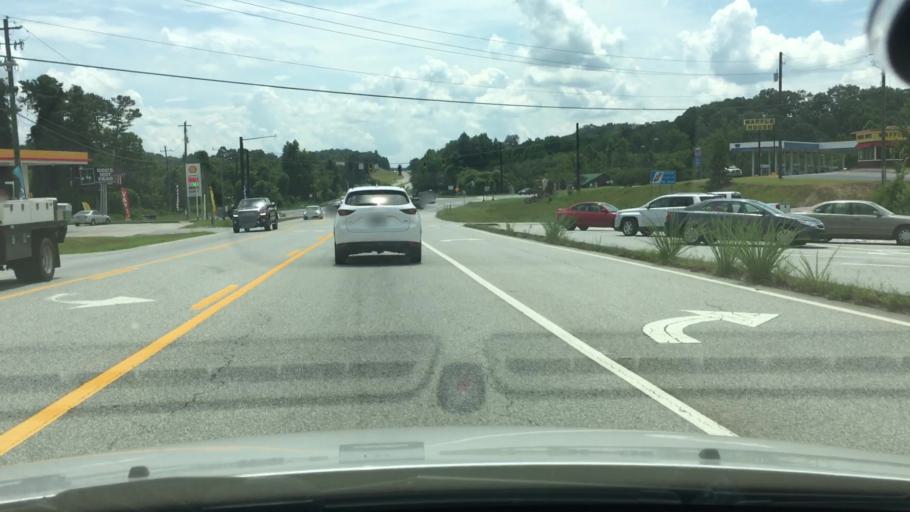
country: US
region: Georgia
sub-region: Lumpkin County
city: Dahlonega
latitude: 34.4700
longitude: -83.9666
